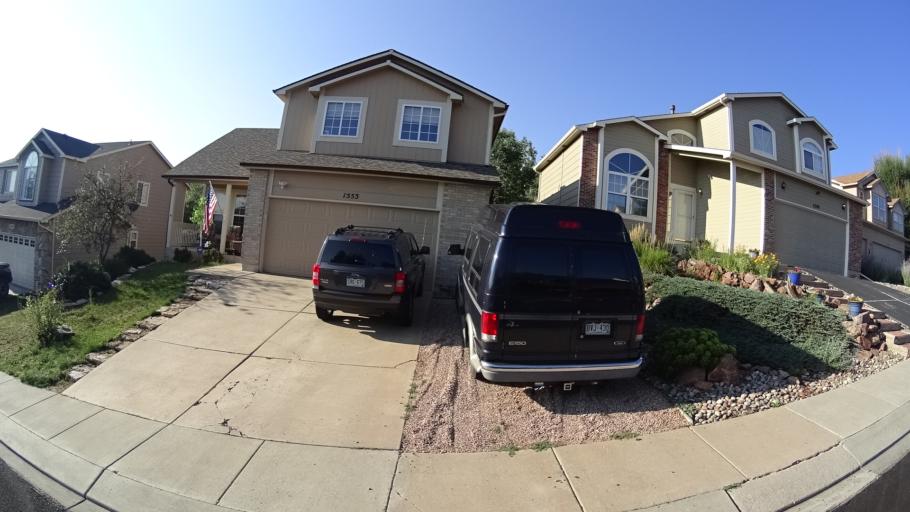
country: US
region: Colorado
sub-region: El Paso County
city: Colorado Springs
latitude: 38.8898
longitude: -104.8574
